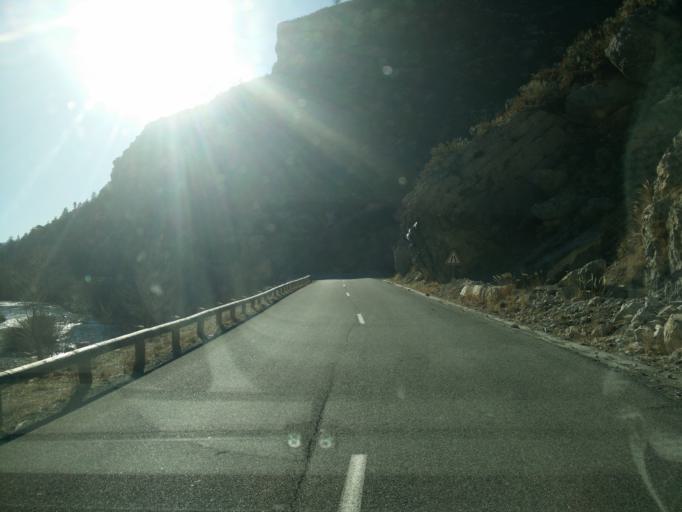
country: FR
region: Provence-Alpes-Cote d'Azur
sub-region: Departement des Alpes-de-Haute-Provence
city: Castellane
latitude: 43.8124
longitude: 6.4367
